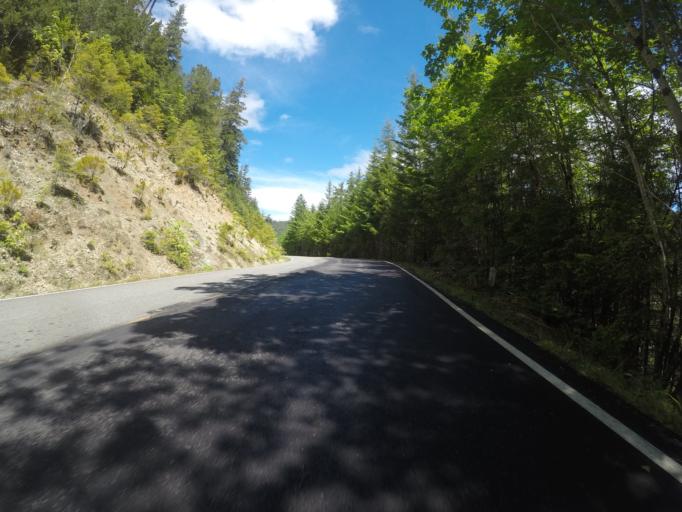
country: US
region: California
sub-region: Del Norte County
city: Bertsch-Oceanview
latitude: 41.7209
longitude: -123.9491
